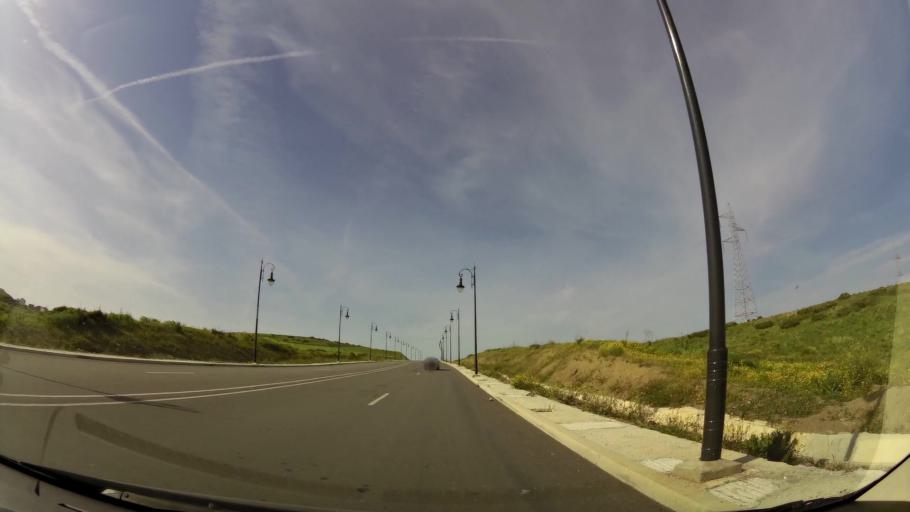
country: MA
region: Tanger-Tetouan
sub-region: Tanger-Assilah
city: Tangier
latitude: 35.7100
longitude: -5.7790
